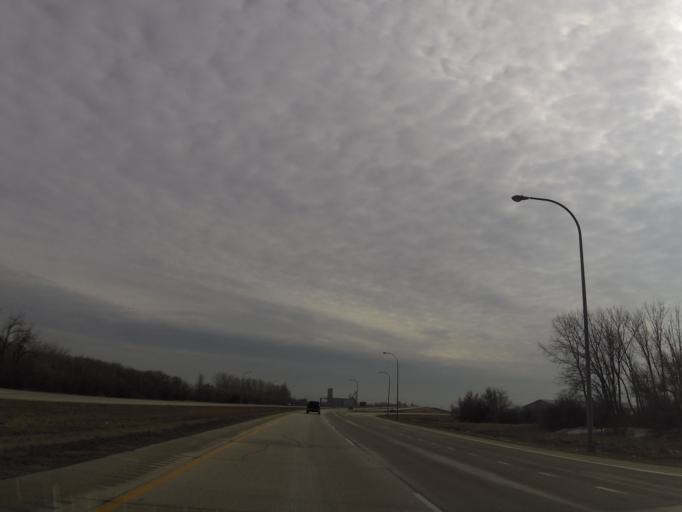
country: US
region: North Dakota
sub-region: Grand Forks County
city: Grand Forks
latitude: 47.9923
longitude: -97.0928
